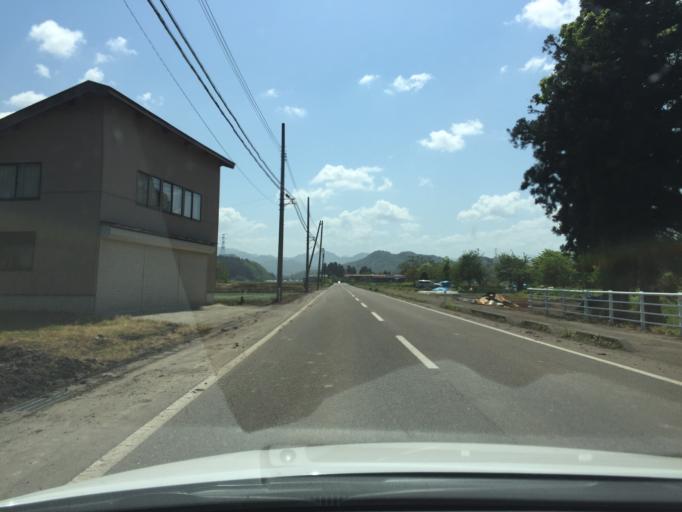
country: JP
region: Niigata
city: Tochio-honcho
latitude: 37.5524
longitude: 139.0805
